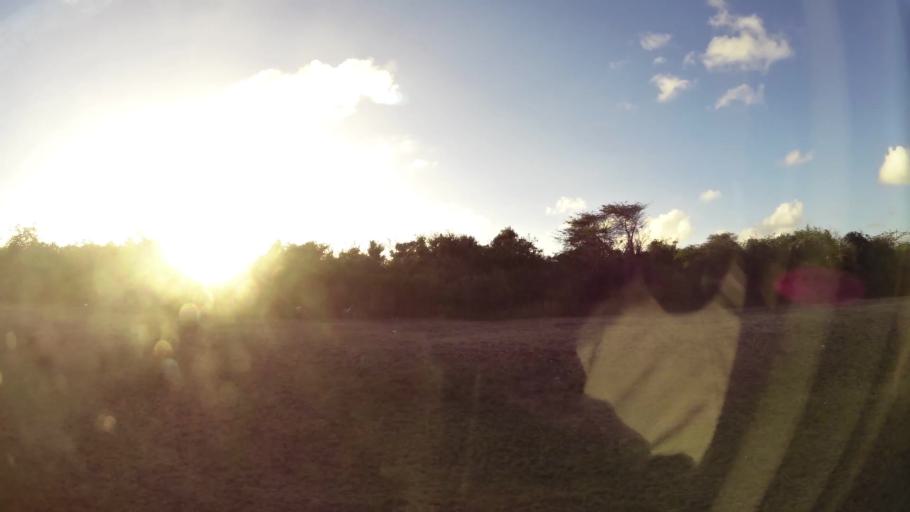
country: AG
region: Saint George
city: Piggotts
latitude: 17.1596
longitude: -61.7982
